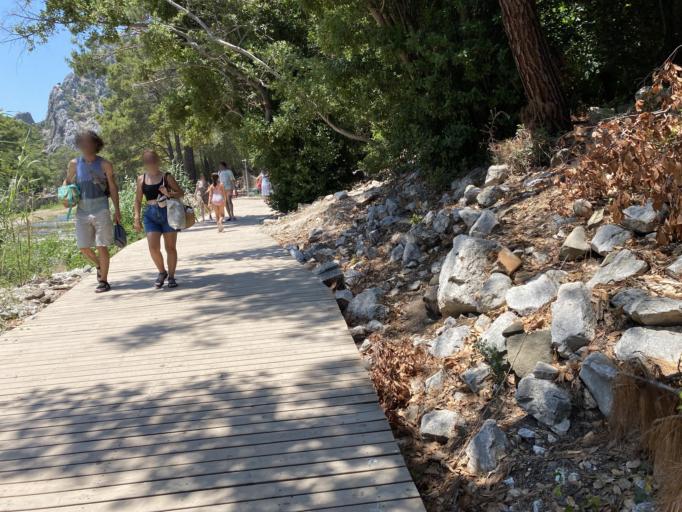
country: TR
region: Antalya
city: Tekirova
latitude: 36.3965
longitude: 30.4747
